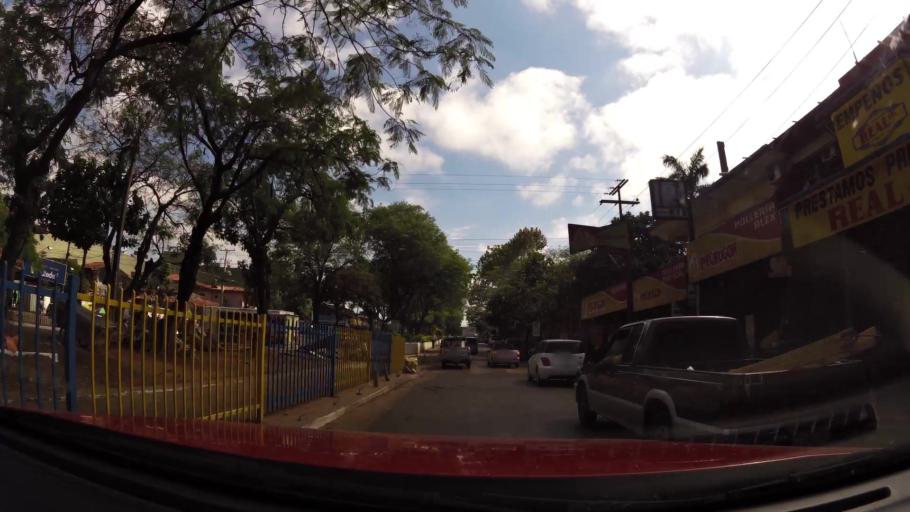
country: PY
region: Central
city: San Lorenzo
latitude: -25.2718
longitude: -57.4863
